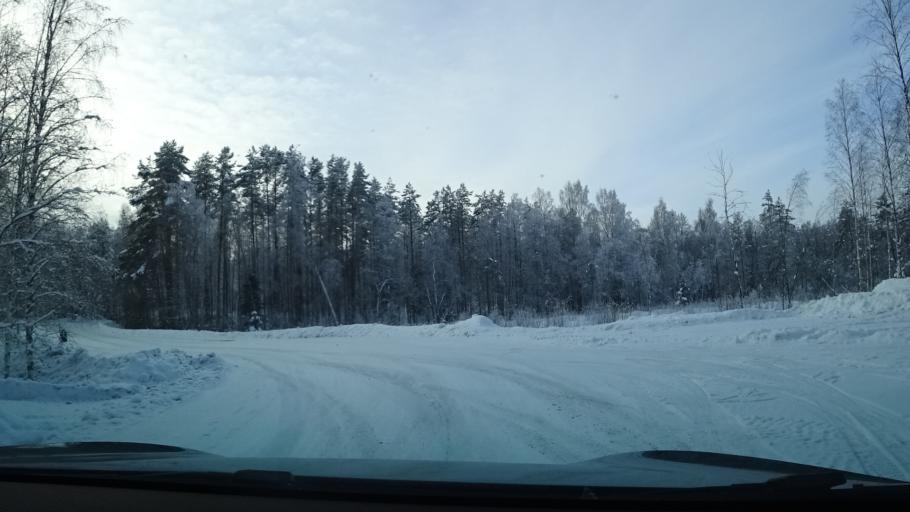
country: FI
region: South Karelia
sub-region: Imatra
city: Rautjaervi
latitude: 61.3260
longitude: 29.1080
